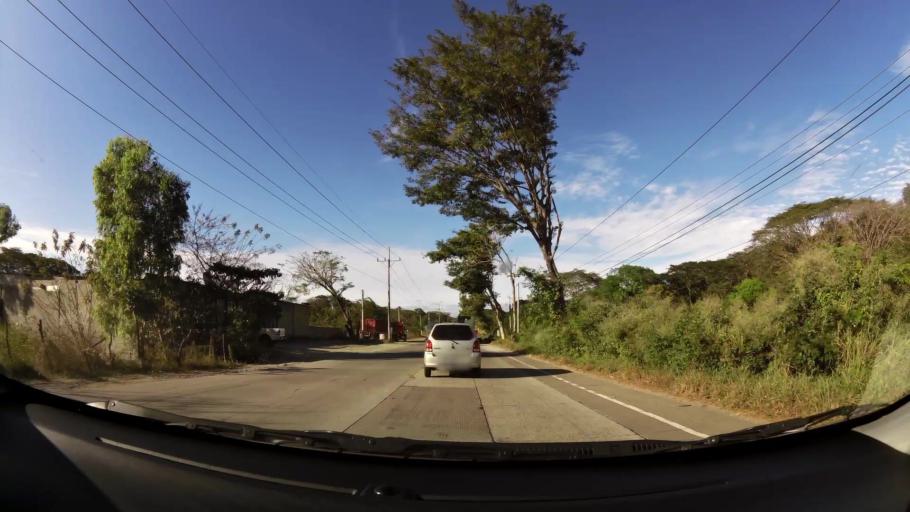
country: SV
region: Santa Ana
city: Metapan
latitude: 14.2810
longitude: -89.4614
